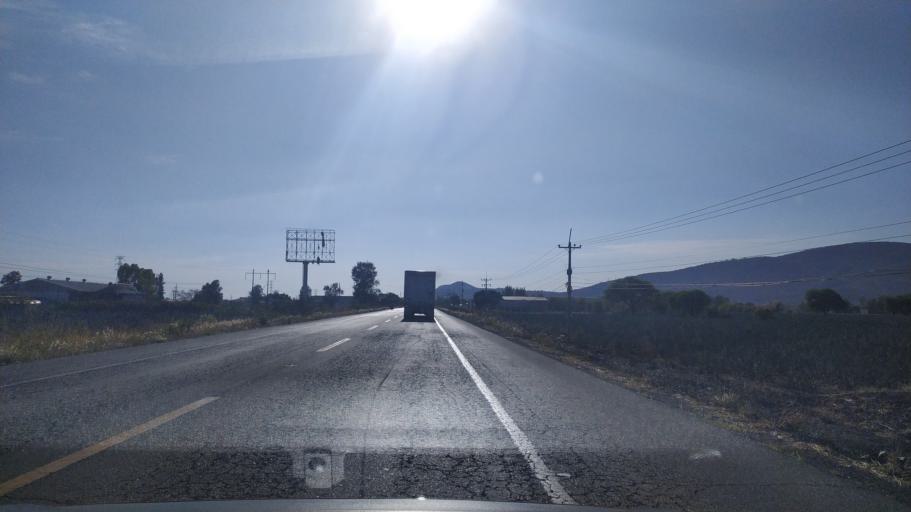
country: MX
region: Jalisco
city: Jamay
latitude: 20.2938
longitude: -102.6557
